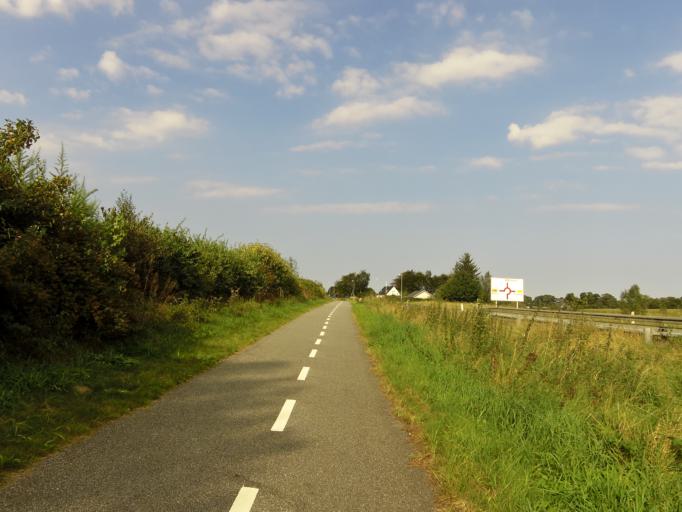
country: DK
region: South Denmark
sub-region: Vejen Kommune
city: Vejen
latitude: 55.4463
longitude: 9.1375
